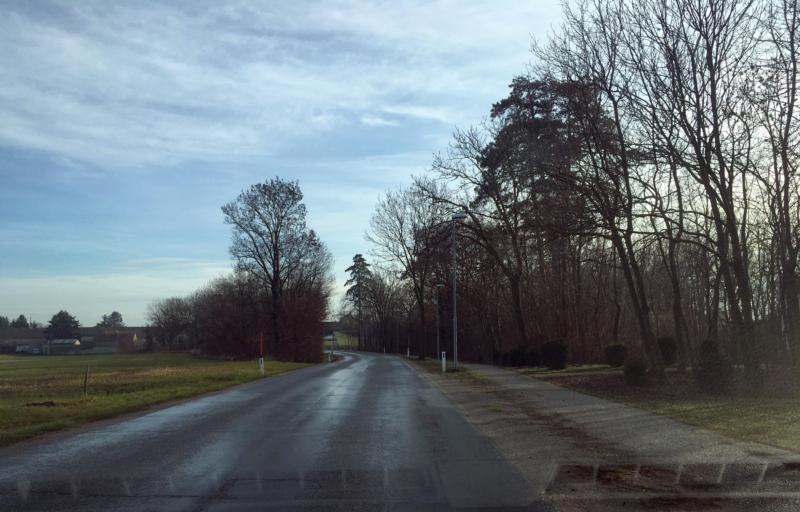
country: AT
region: Lower Austria
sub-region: Politischer Bezirk Ganserndorf
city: Orth an der Donau
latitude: 48.1833
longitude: 16.7347
